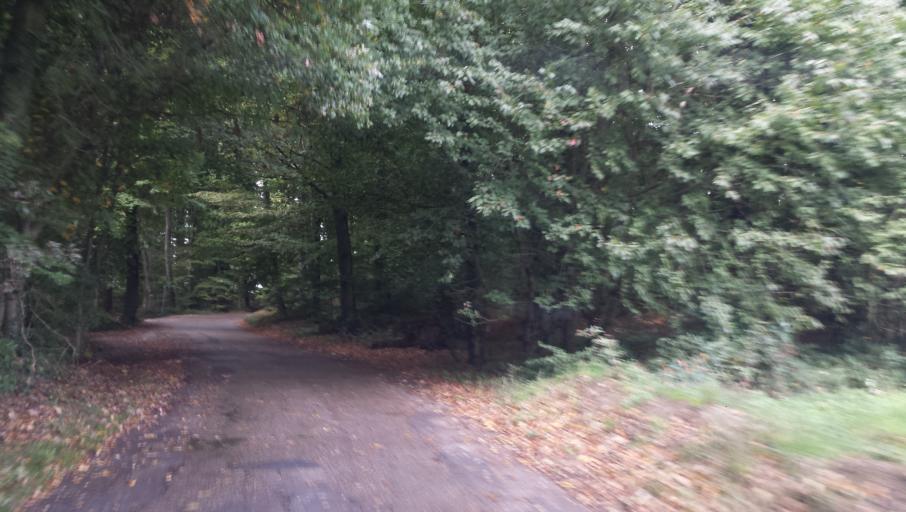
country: DE
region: Hesse
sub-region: Regierungsbezirk Darmstadt
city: Birkenau
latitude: 49.5141
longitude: 8.7166
